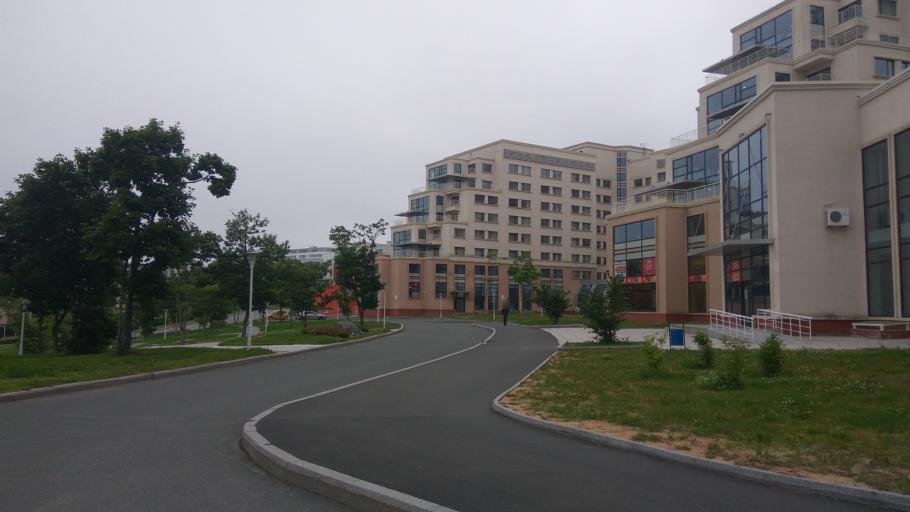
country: RU
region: Primorskiy
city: Russkiy
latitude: 43.0310
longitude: 131.8866
